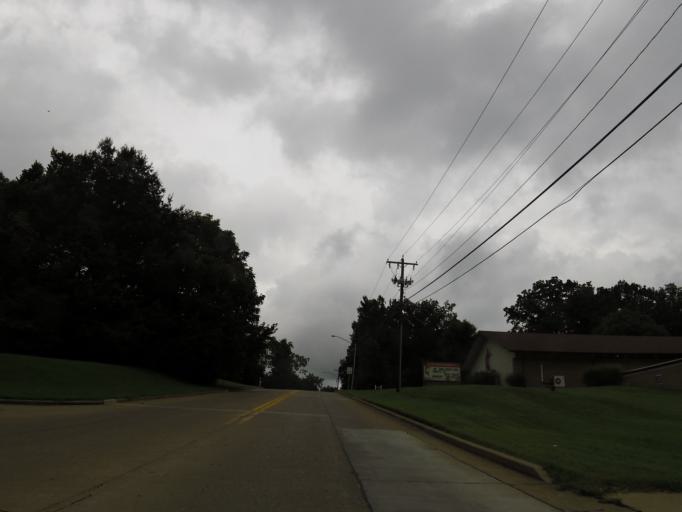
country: US
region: Missouri
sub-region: Cape Girardeau County
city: Cape Girardeau
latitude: 37.3243
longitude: -89.5513
